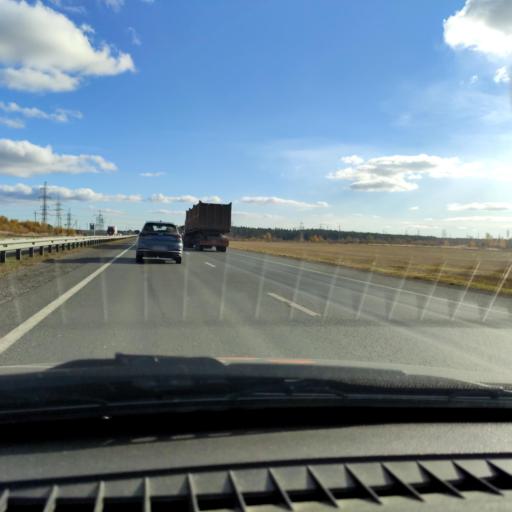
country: RU
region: Samara
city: Zhigulevsk
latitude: 53.5483
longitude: 49.5095
